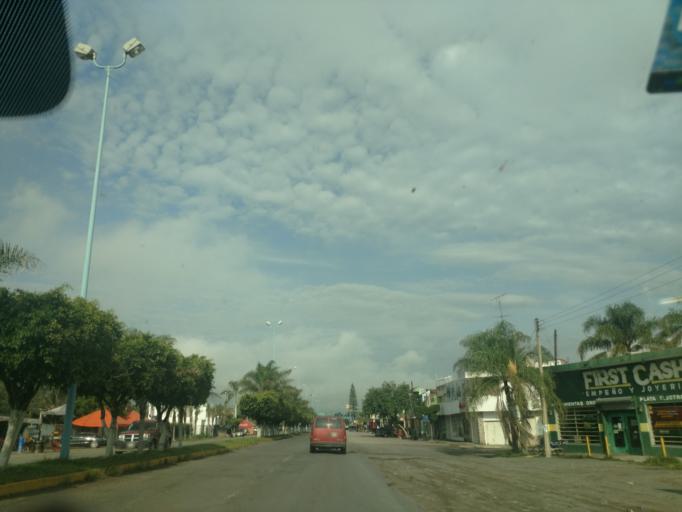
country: MX
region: Jalisco
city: Ameca
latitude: 20.5374
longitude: -104.0390
